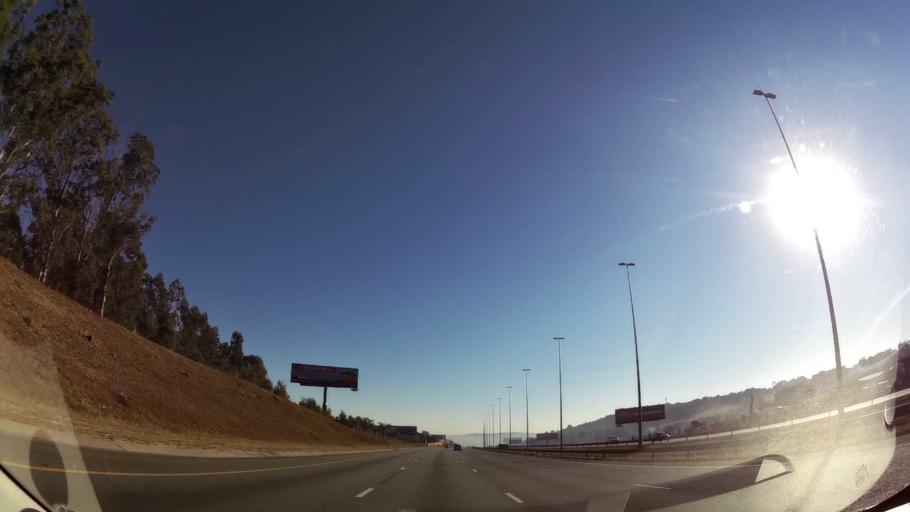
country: ZA
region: Gauteng
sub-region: City of Tshwane Metropolitan Municipality
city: Centurion
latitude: -25.9004
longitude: 28.2548
